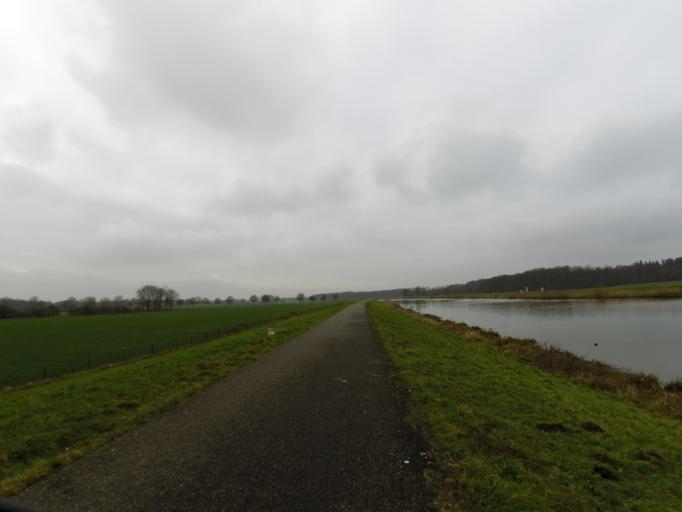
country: NL
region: Gelderland
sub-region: Gemeente Doetinchem
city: Doetinchem
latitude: 51.9949
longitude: 6.2164
